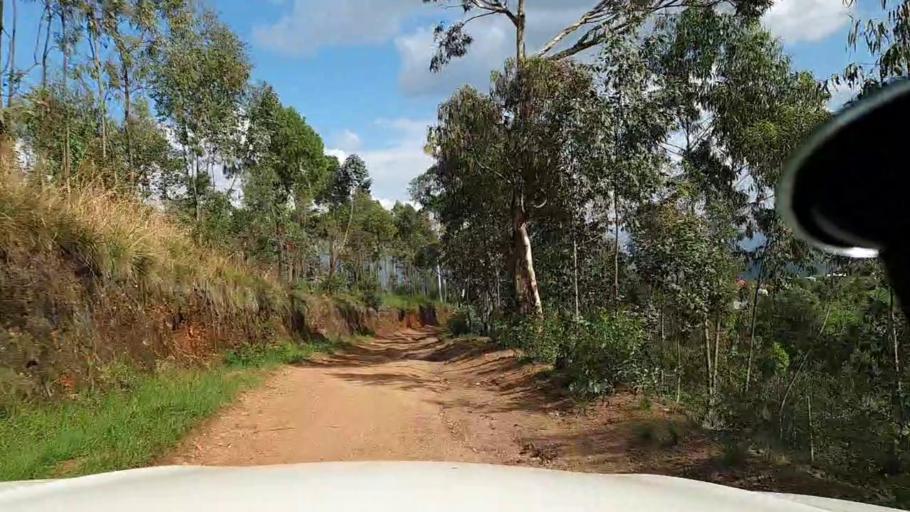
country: RW
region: Kigali
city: Kigali
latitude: -1.7897
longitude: 29.8408
